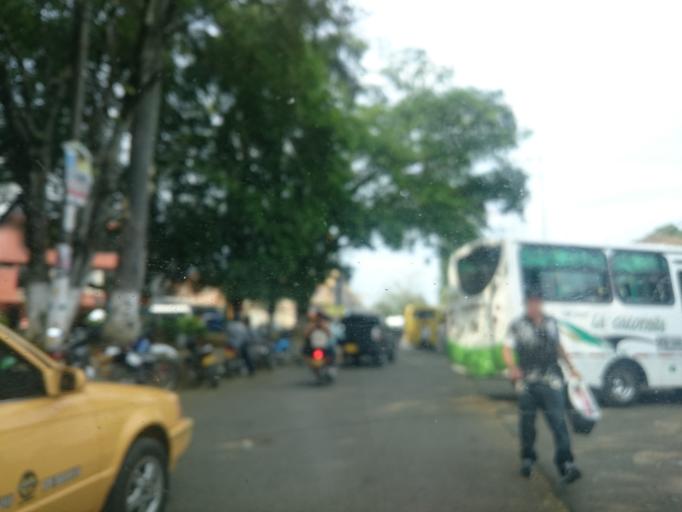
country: CO
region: Cauca
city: Santander de Quilichao
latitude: 3.0089
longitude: -76.4862
